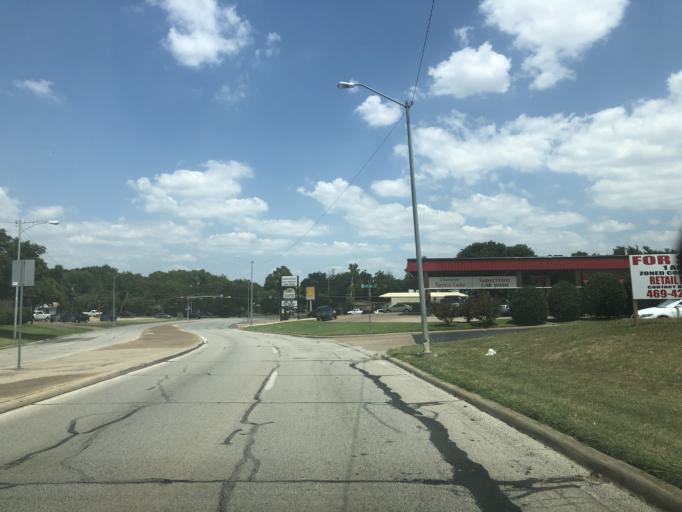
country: US
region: Texas
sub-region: Dallas County
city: Grand Prairie
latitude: 32.7474
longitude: -97.0168
